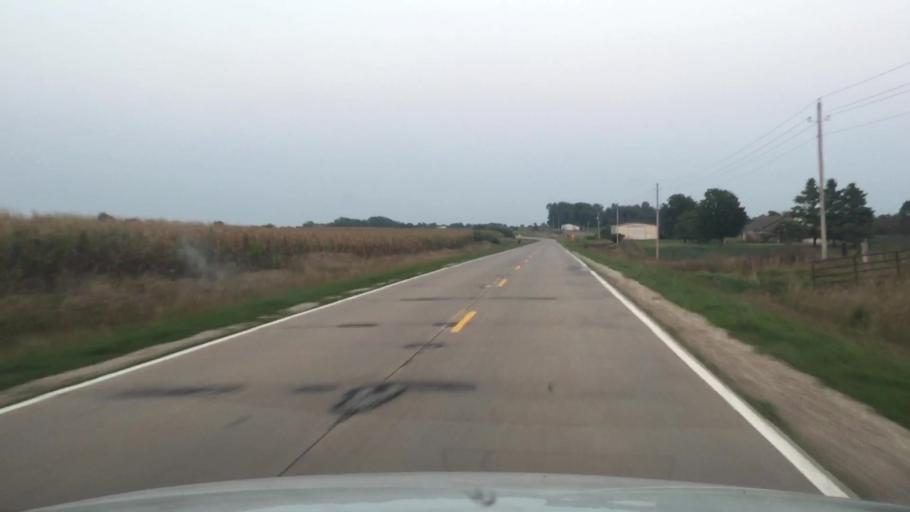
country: US
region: Iowa
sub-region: Clarke County
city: Osceola
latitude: 41.1875
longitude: -93.6824
